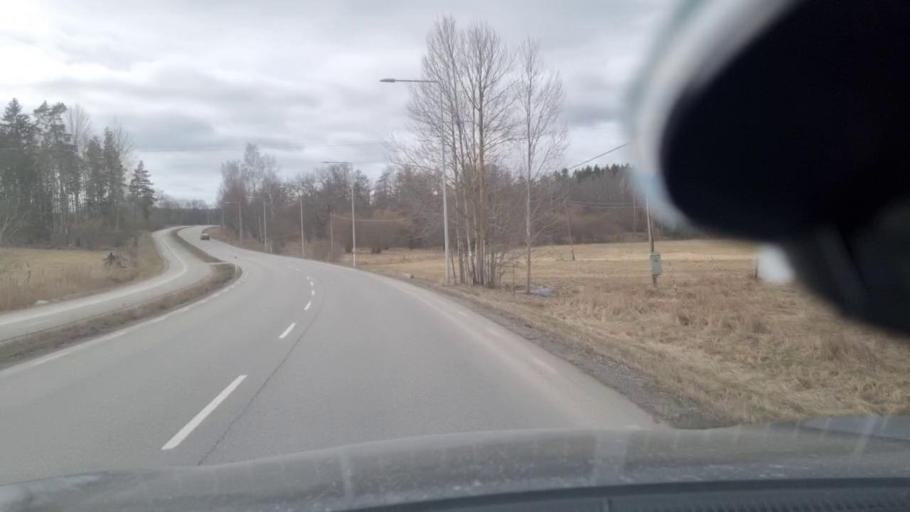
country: SE
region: Stockholm
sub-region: Jarfalla Kommun
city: Jakobsberg
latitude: 59.4265
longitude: 17.7917
